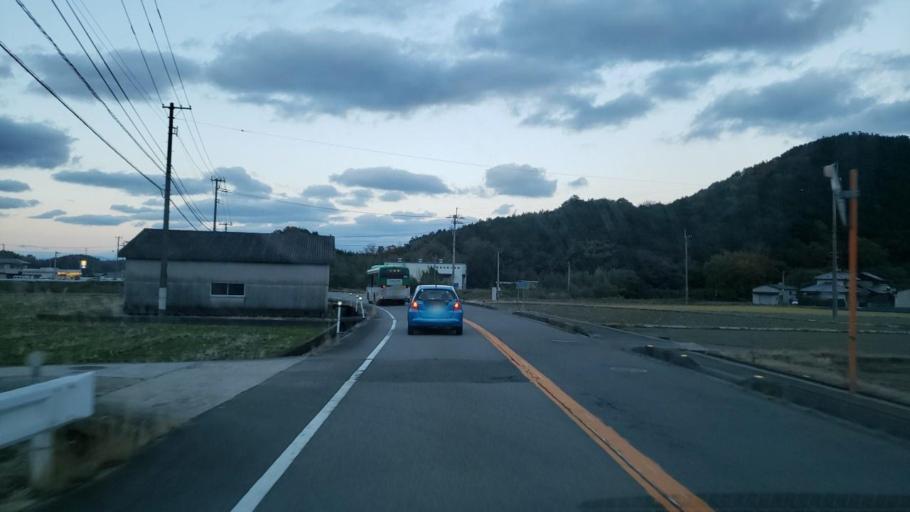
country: JP
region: Tokushima
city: Kamojimacho-jogejima
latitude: 34.2213
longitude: 134.3393
